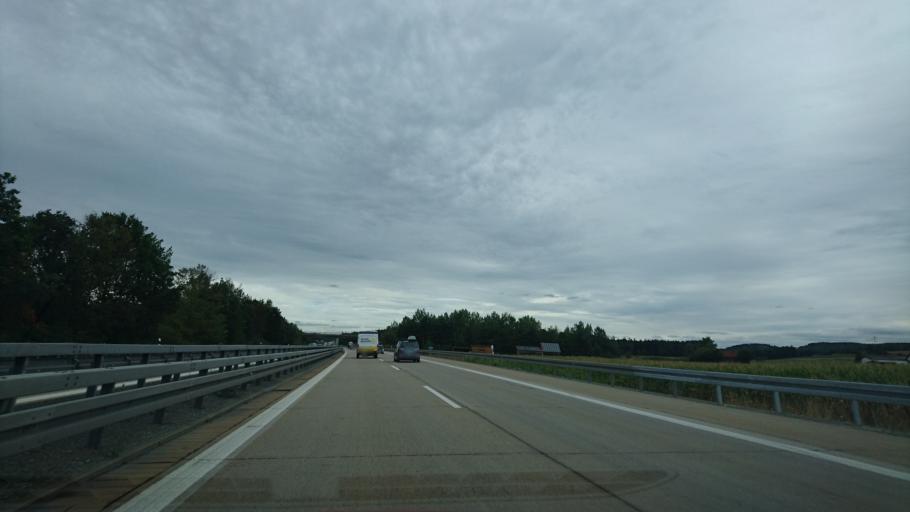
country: DE
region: Bavaria
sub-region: Upper Palatinate
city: Pirk
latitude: 49.6164
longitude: 12.1526
